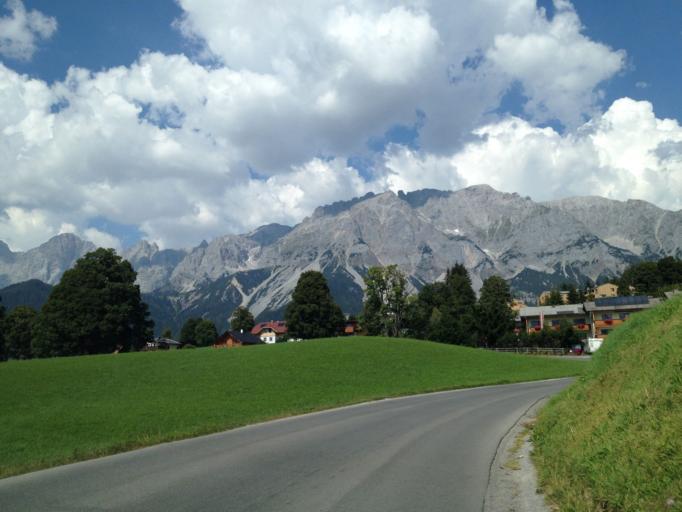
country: AT
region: Styria
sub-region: Politischer Bezirk Liezen
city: Schladming
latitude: 47.4097
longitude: 13.6357
